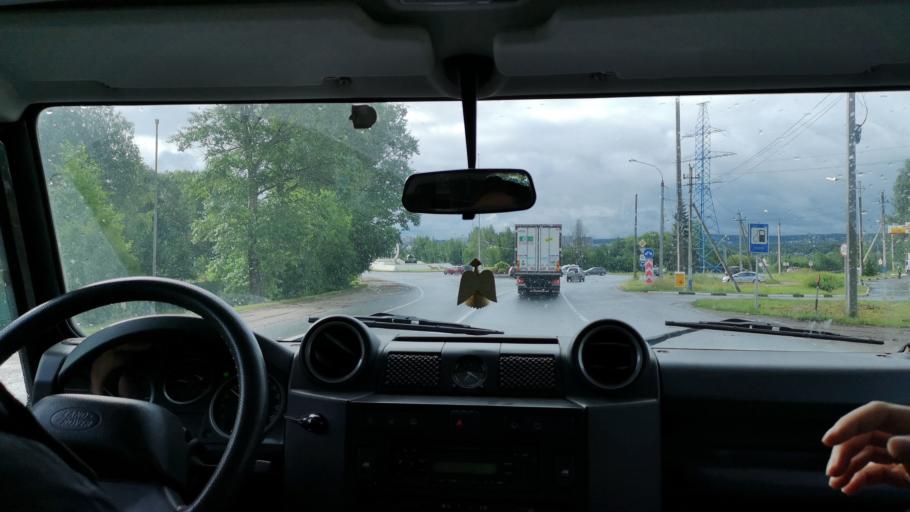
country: RU
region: Moskovskaya
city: Dmitrov
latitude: 56.3588
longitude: 37.4872
